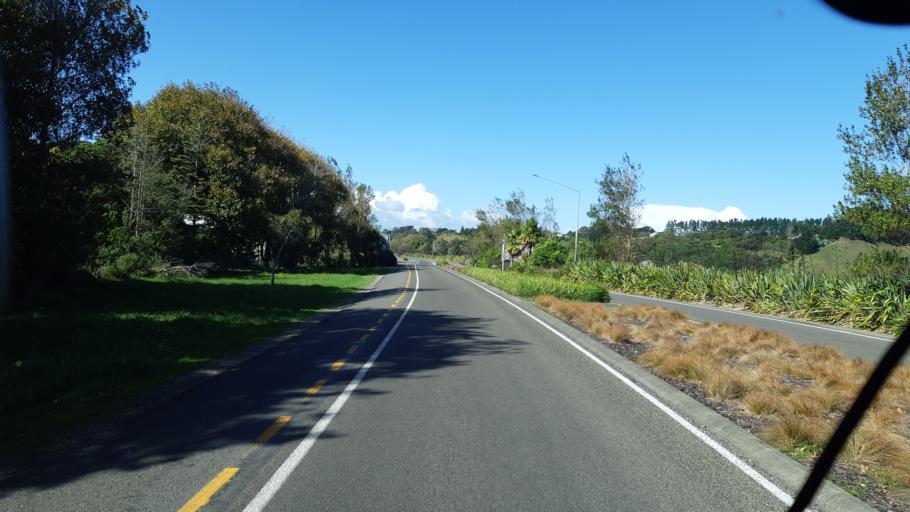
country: NZ
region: Manawatu-Wanganui
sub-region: Wanganui District
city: Wanganui
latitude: -39.9490
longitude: 175.0519
